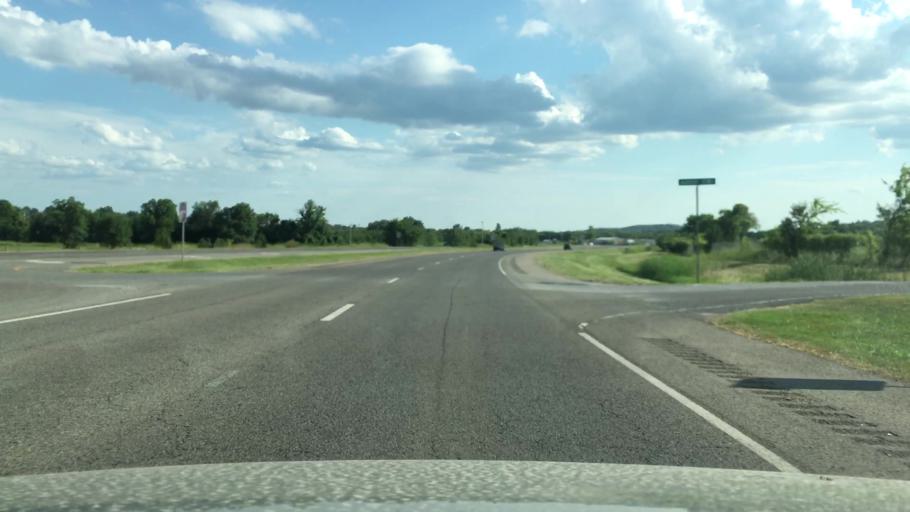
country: US
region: Oklahoma
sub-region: Cherokee County
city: Tahlequah
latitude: 35.9257
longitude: -95.0012
